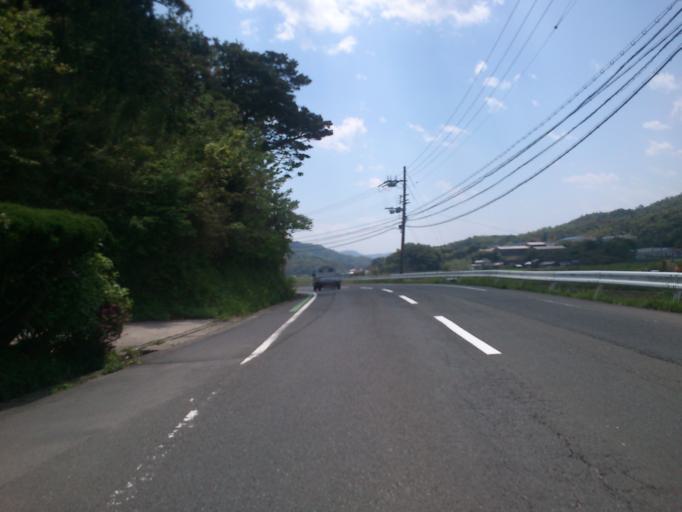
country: JP
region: Kyoto
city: Miyazu
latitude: 35.7269
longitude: 135.1037
